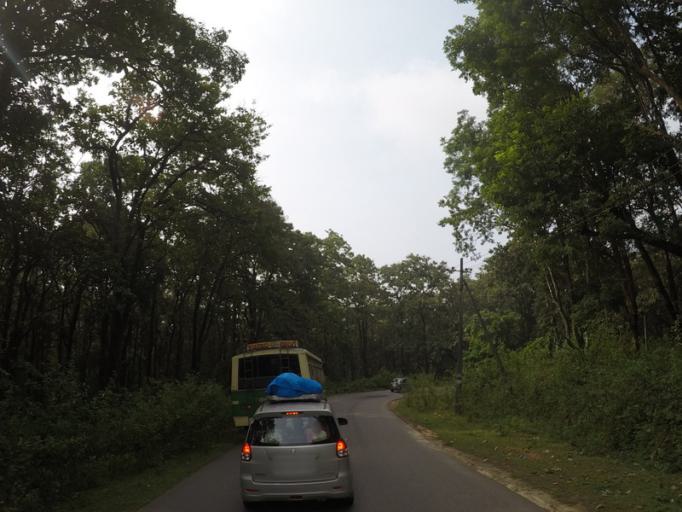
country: IN
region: Karnataka
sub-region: Chikmagalur
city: Koppa
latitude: 13.3540
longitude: 75.4964
